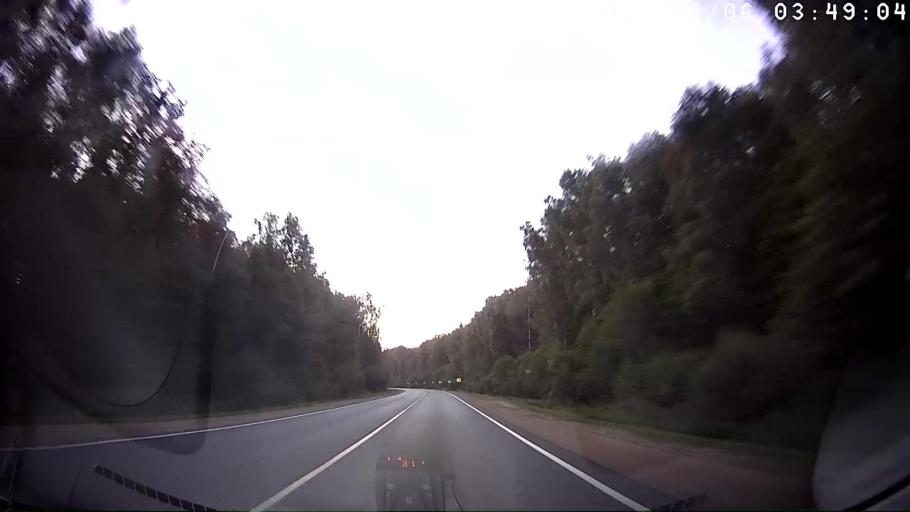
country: RU
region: Tatarstan
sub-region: Zelenodol'skiy Rayon
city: Zelenodolsk
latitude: 55.8819
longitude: 48.5044
